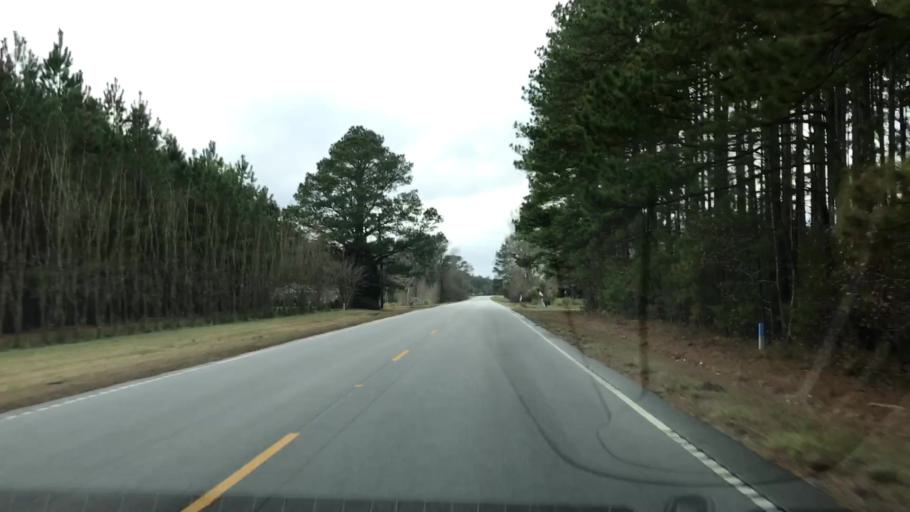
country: US
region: South Carolina
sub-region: Williamsburg County
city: Andrews
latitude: 33.2827
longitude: -79.7224
